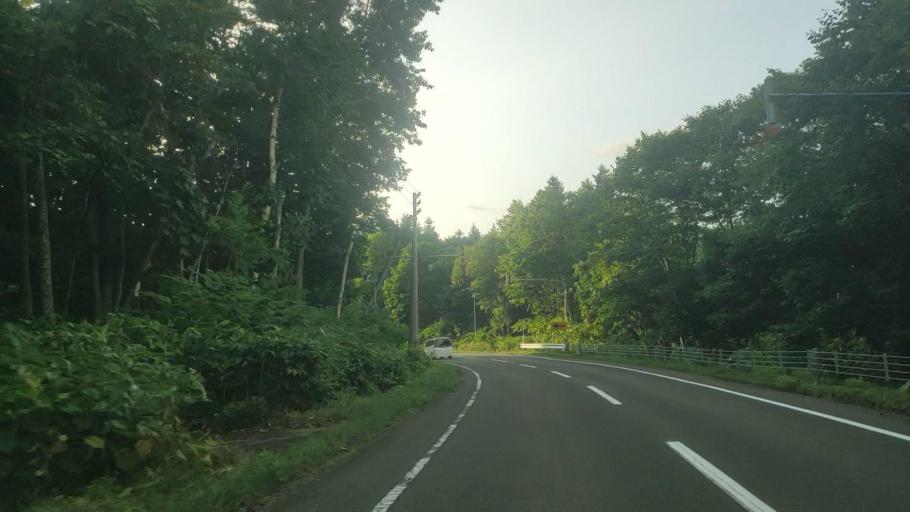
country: JP
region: Hokkaido
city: Bibai
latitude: 43.1773
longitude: 142.0695
